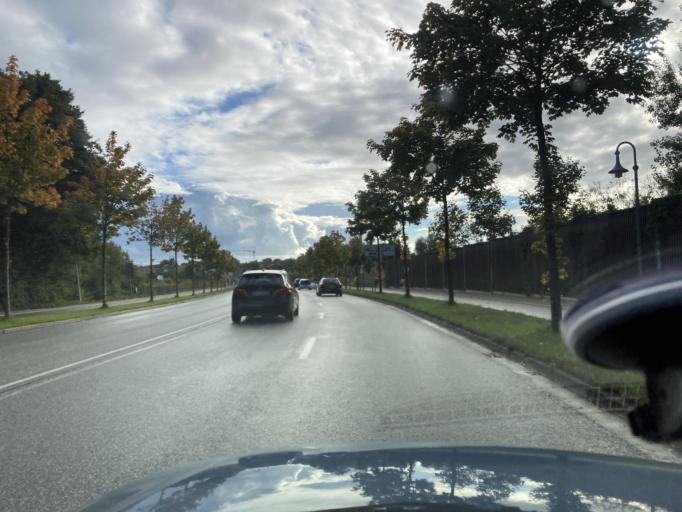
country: DE
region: Schleswig-Holstein
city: Rendsburg
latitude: 54.3119
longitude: 9.6647
